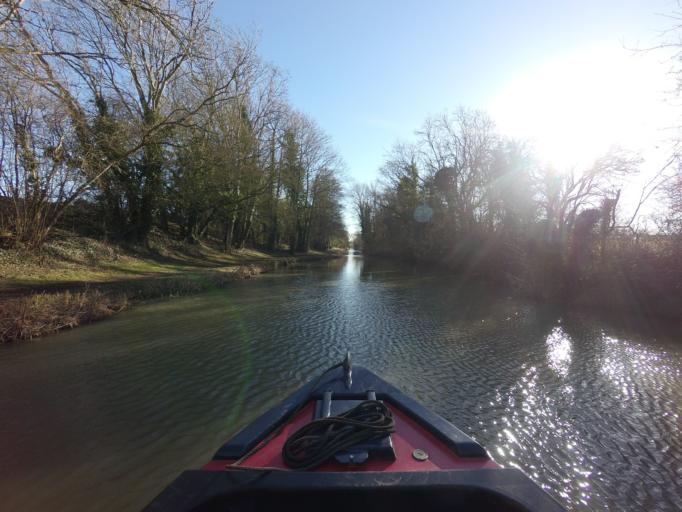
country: GB
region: England
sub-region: Northamptonshire
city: Bugbrooke
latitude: 52.2099
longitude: -1.0215
